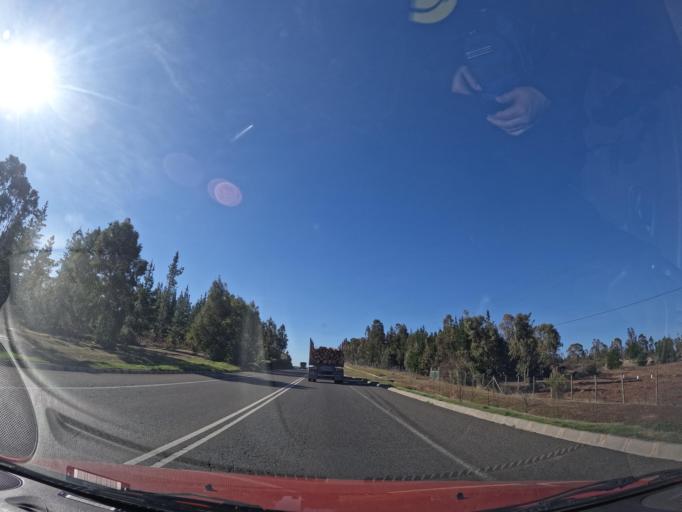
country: CL
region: Maule
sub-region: Provincia de Cauquenes
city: Cauquenes
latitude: -35.9297
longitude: -72.1870
